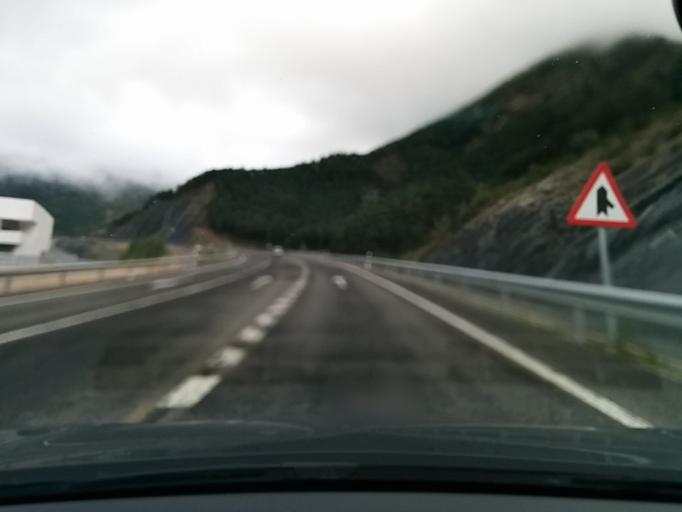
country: ES
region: Aragon
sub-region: Provincia de Huesca
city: Arguis
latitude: 42.3073
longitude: -0.4246
